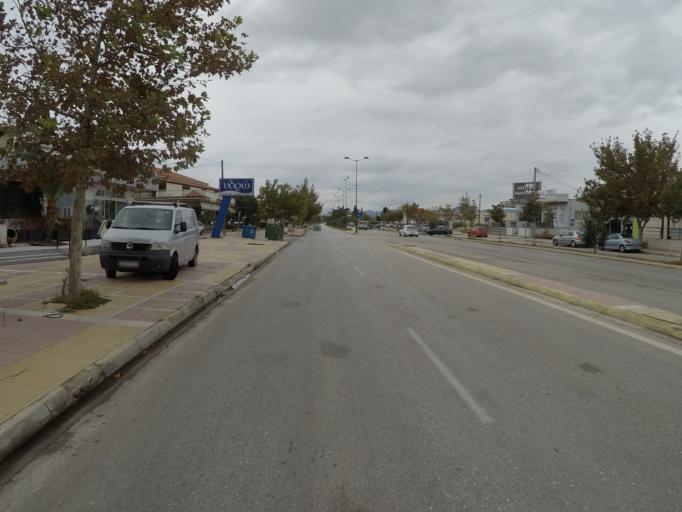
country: GR
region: Peloponnese
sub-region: Nomos Korinthias
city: Loutraki
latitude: 37.9620
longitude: 22.9789
